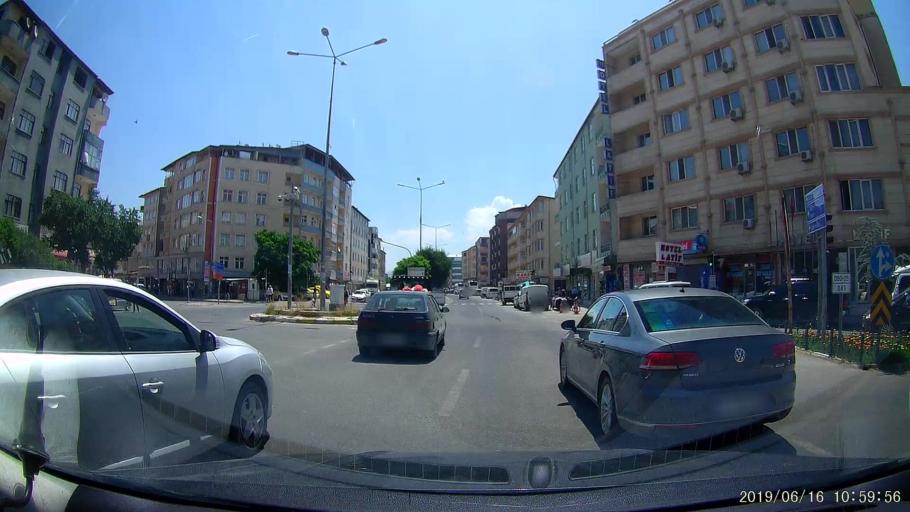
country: TR
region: Igdir
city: Igdir
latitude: 39.9195
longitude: 44.0411
